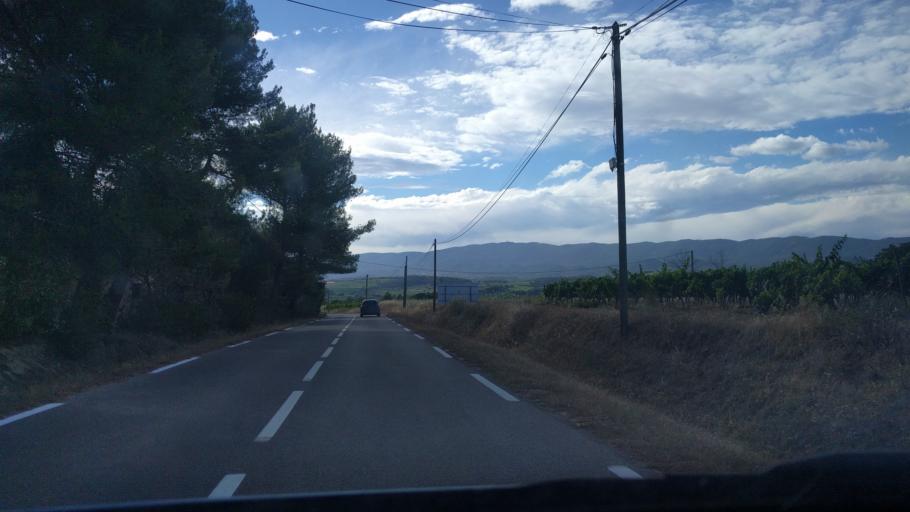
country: FR
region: Provence-Alpes-Cote d'Azur
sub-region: Departement du Vaucluse
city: Grambois
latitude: 43.7276
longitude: 5.5795
